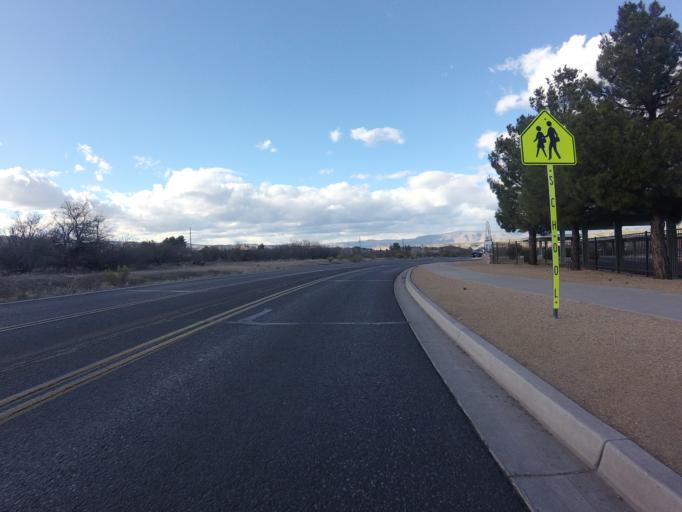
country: US
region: Arizona
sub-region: Yavapai County
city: Cottonwood
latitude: 34.7414
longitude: -112.0281
